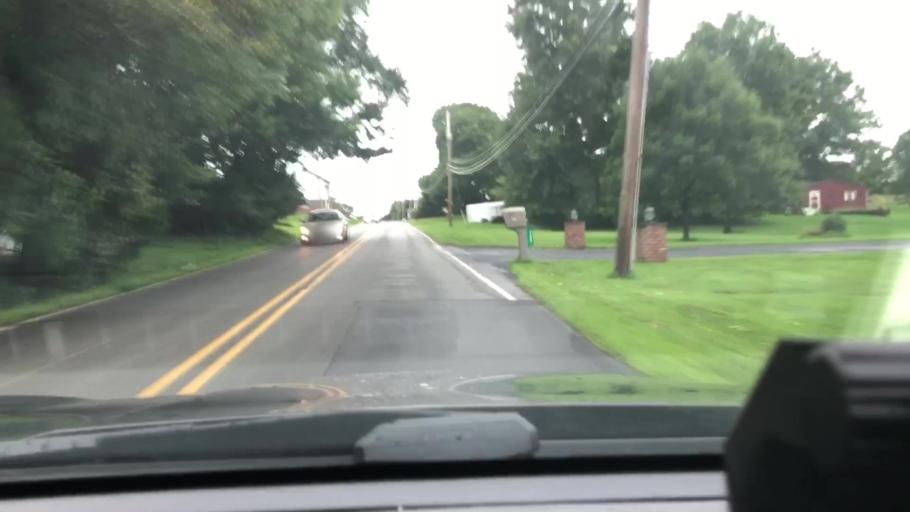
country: US
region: Pennsylvania
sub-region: Montgomery County
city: Gilbertsville
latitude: 40.3071
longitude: -75.6155
